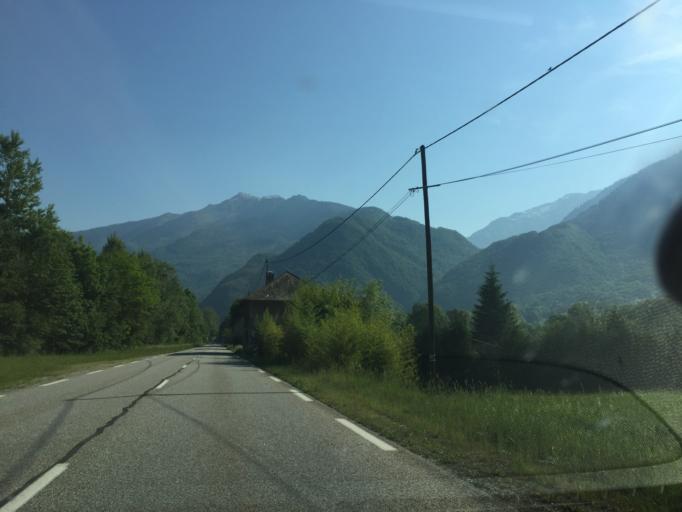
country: FR
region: Rhone-Alpes
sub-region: Departement de la Savoie
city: Aiton
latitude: 45.5024
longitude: 6.3050
